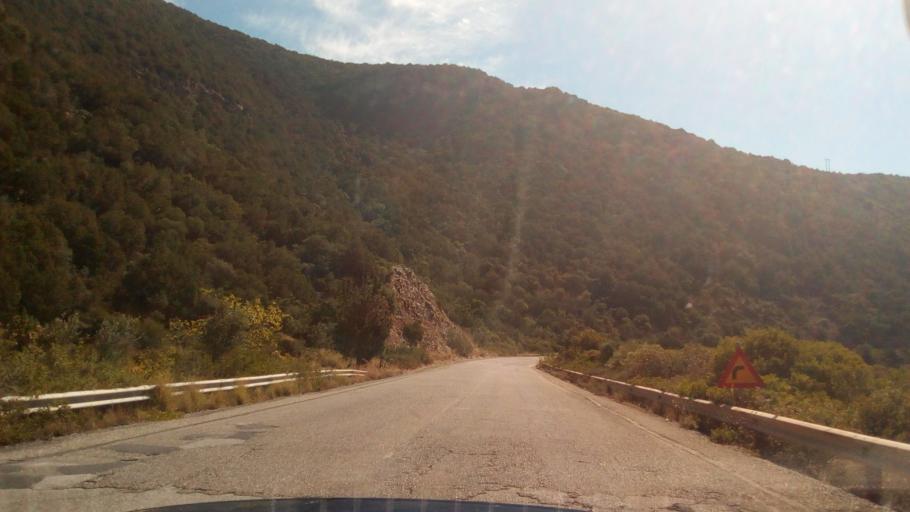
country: GR
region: West Greece
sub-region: Nomos Achaias
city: Selianitika
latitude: 38.3764
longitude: 22.0964
